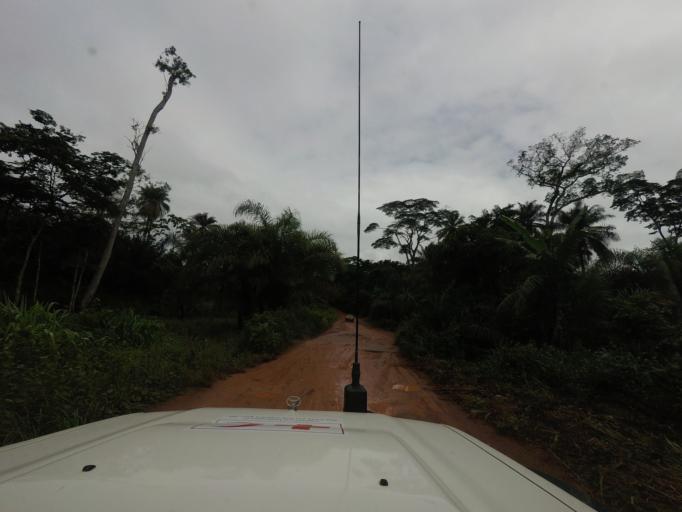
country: GN
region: Nzerekore
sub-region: Nzerekore Prefecture
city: Nzerekore
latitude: 7.7302
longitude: -8.8540
